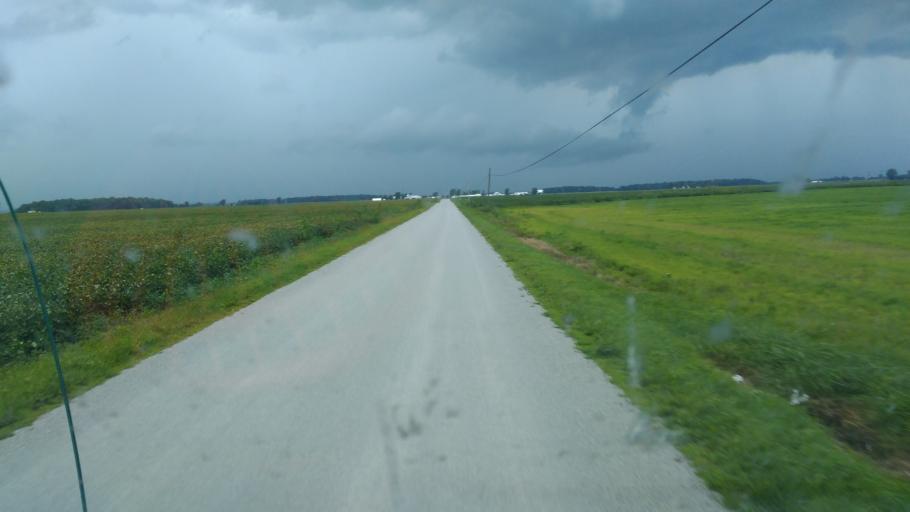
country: US
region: Ohio
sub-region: Hardin County
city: Kenton
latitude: 40.6676
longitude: -83.5146
